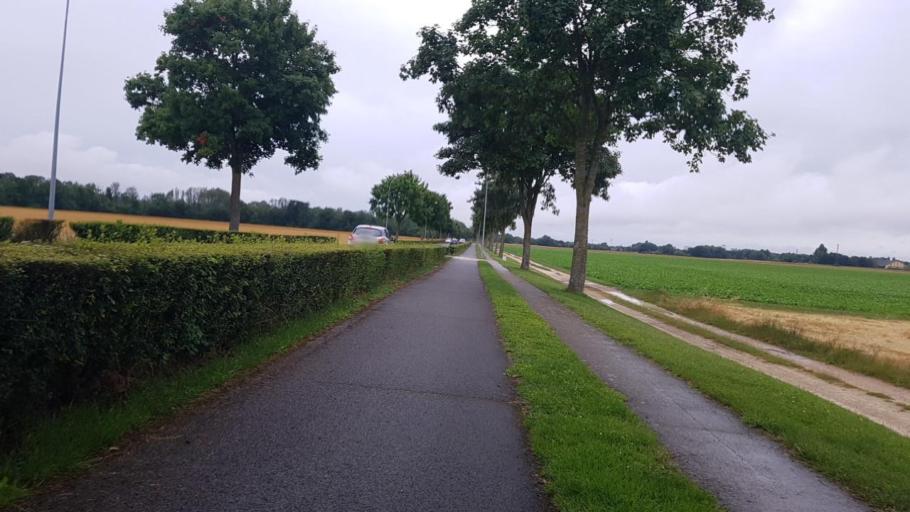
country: FR
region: Champagne-Ardenne
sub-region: Departement de la Marne
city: Sarry
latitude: 48.9241
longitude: 4.3989
